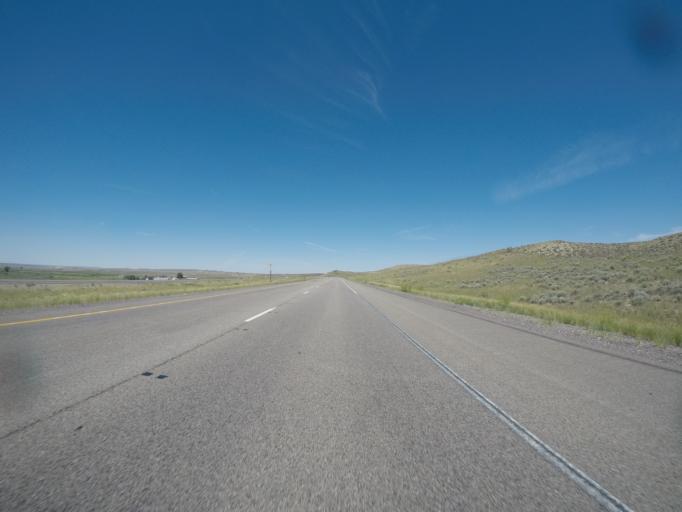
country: US
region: Wyoming
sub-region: Carbon County
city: Saratoga
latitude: 41.7420
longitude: -106.7645
